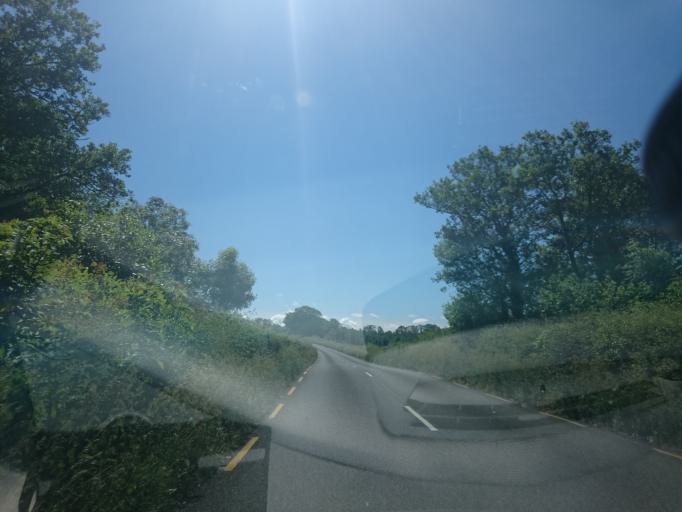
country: IE
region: Leinster
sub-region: Kilkenny
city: Graiguenamanagh
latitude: 52.5685
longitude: -6.9528
